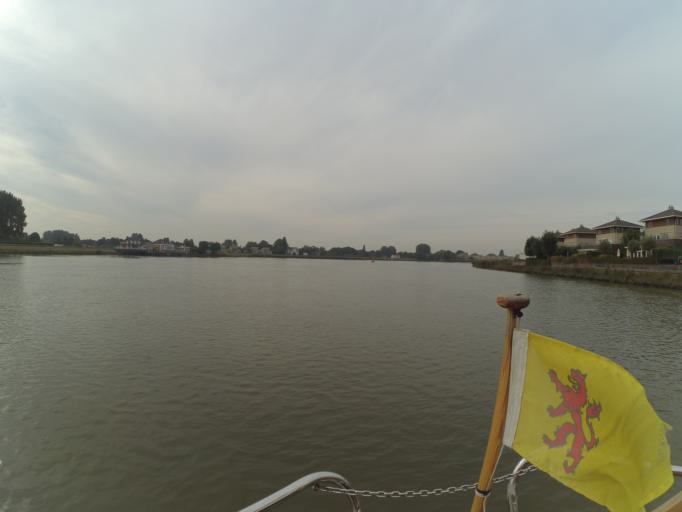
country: NL
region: South Holland
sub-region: Gemeente Krimpen aan den IJssel
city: Krimpen aan den IJssel
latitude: 51.9272
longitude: 4.6143
